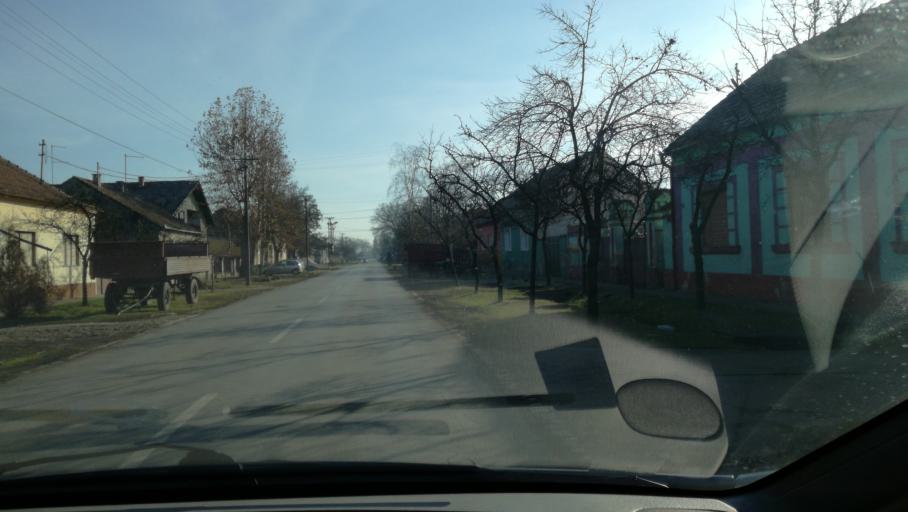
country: RS
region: Autonomna Pokrajina Vojvodina
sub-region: Severnobanatski Okrug
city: Kikinda
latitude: 45.8231
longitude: 20.4644
